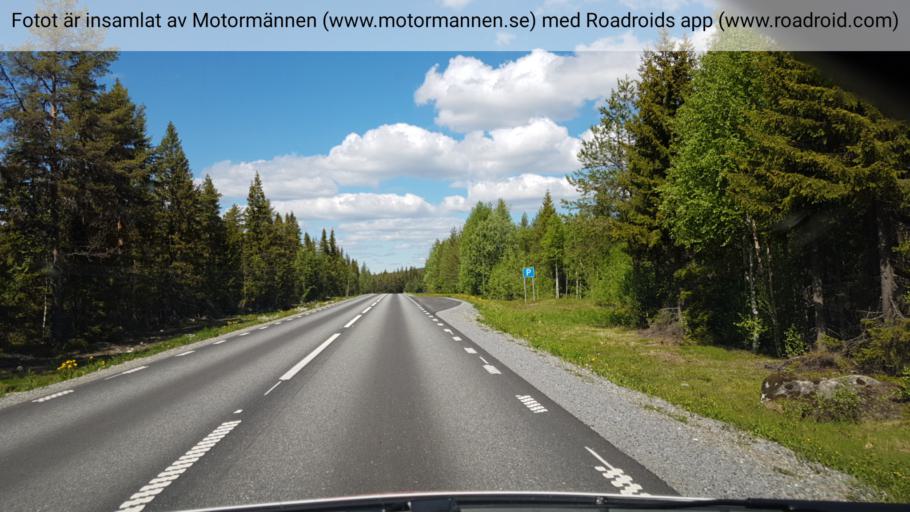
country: SE
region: Vaesterbotten
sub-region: Vilhelmina Kommun
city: Vilhelmina
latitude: 64.6966
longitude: 16.7145
